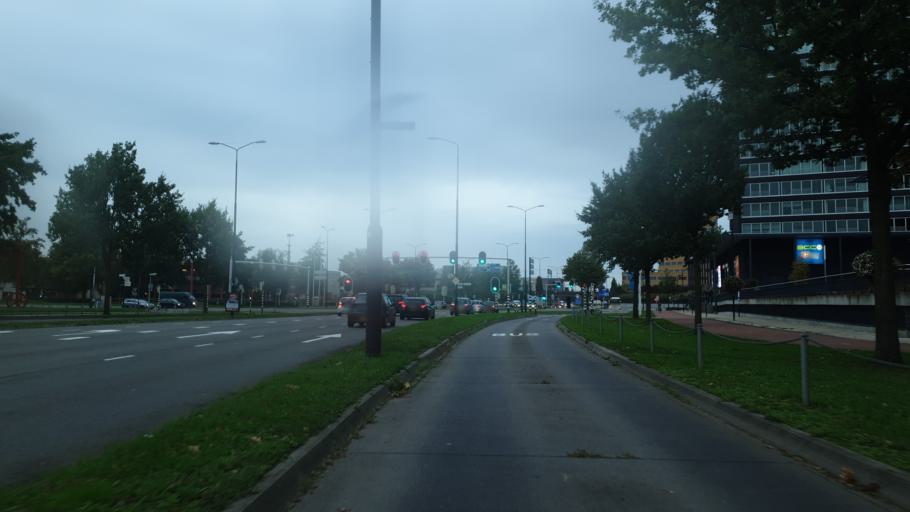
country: NL
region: Gelderland
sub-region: Gemeente Nijmegen
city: Lindenholt
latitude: 51.8214
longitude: 5.7933
